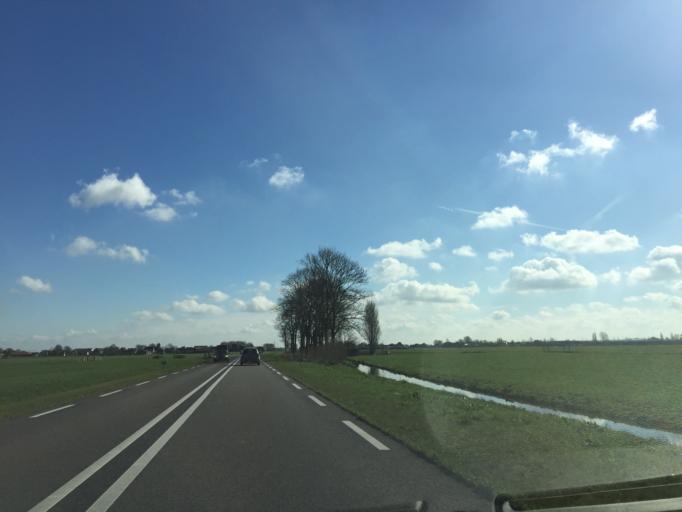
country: NL
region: South Holland
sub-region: Gemeente Leiderdorp
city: Leiderdorp
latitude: 52.1844
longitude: 4.5750
